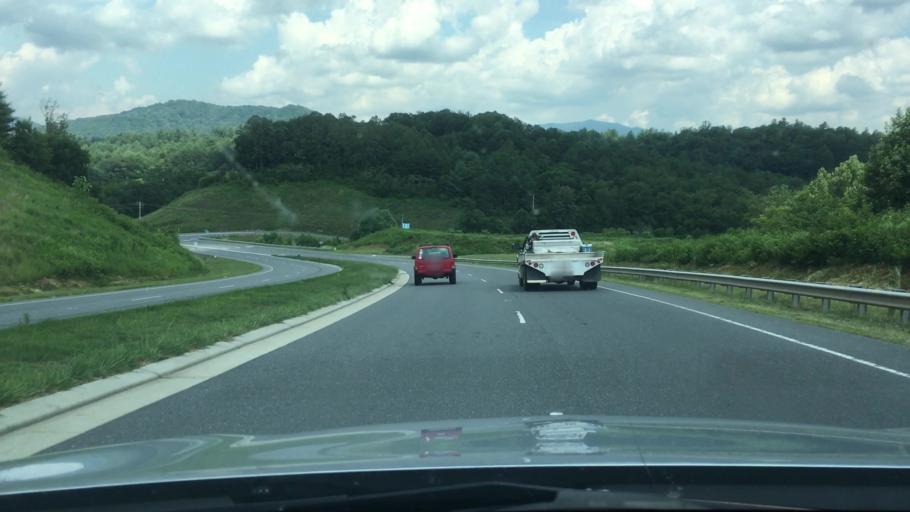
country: US
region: North Carolina
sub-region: Madison County
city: Mars Hill
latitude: 35.8385
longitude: -82.5123
